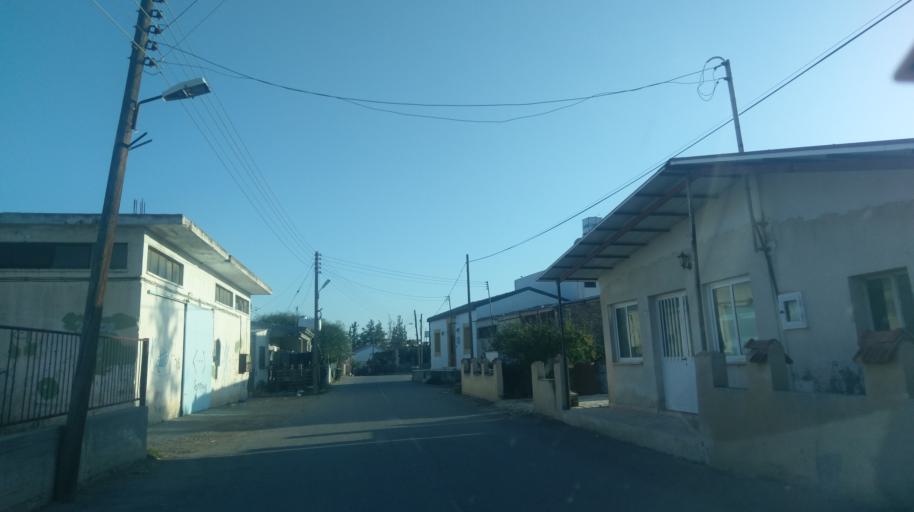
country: CY
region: Ammochostos
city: Lefkonoiko
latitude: 35.2239
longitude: 33.6176
